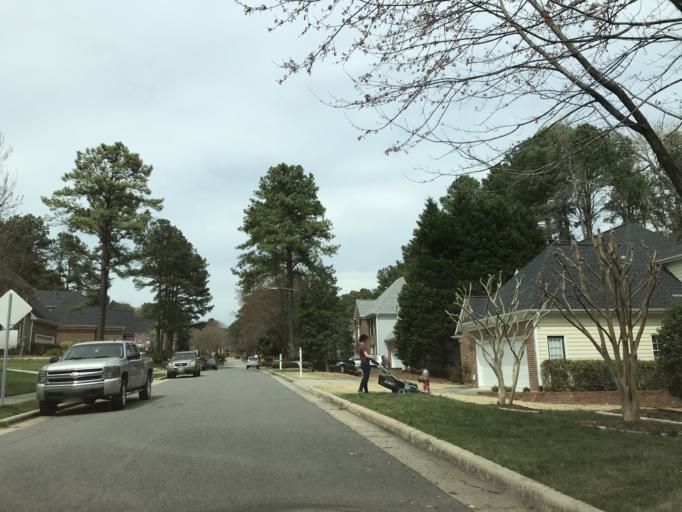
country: US
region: North Carolina
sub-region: Wake County
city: West Raleigh
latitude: 35.8848
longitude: -78.6851
